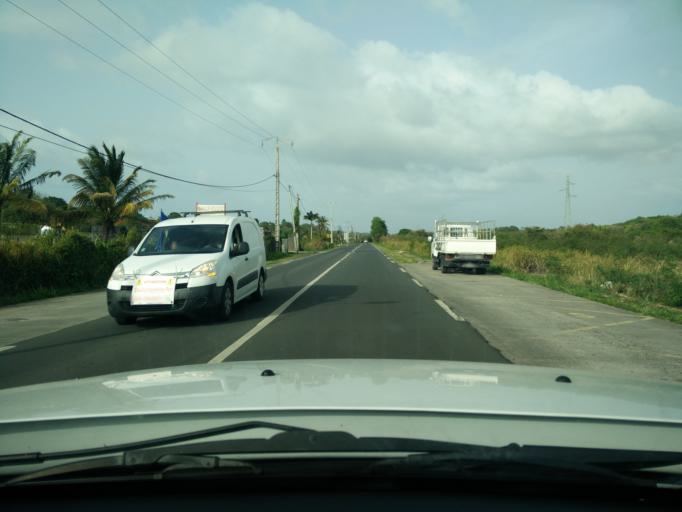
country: GP
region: Guadeloupe
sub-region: Guadeloupe
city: Saint-Francois
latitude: 16.2571
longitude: -61.3085
